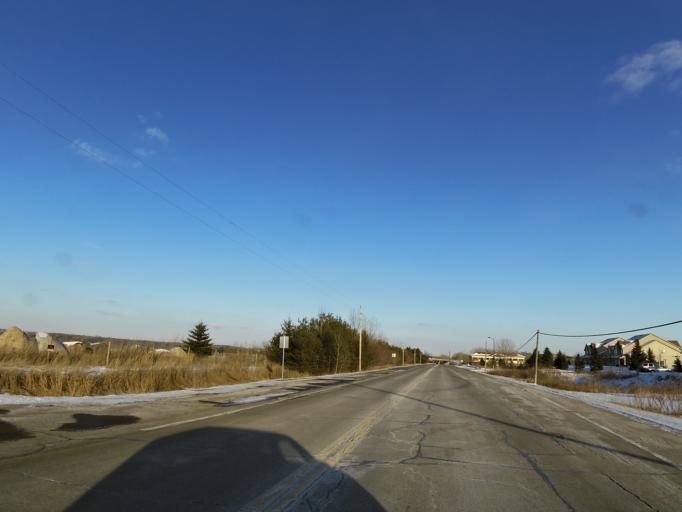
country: US
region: Minnesota
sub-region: Dakota County
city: Lakeville
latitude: 44.6523
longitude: -93.3041
